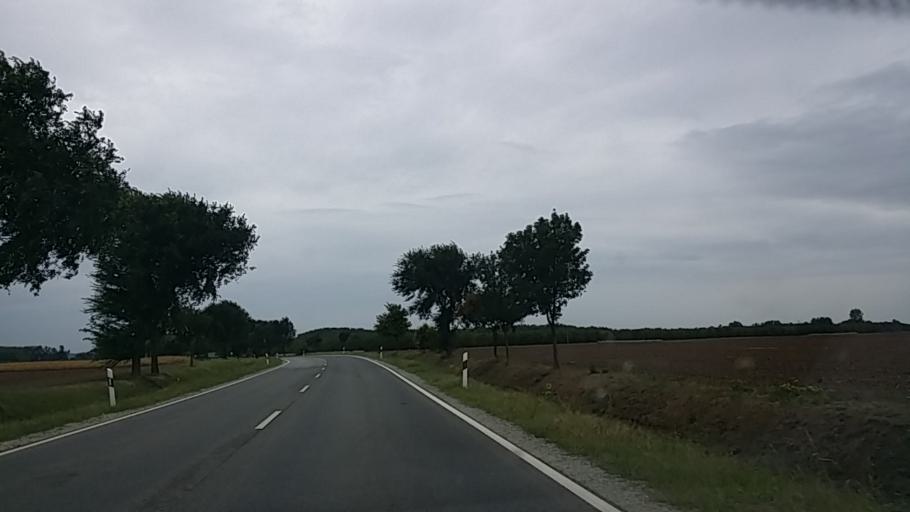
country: HU
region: Gyor-Moson-Sopron
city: Fertod
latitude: 47.5962
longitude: 16.7907
